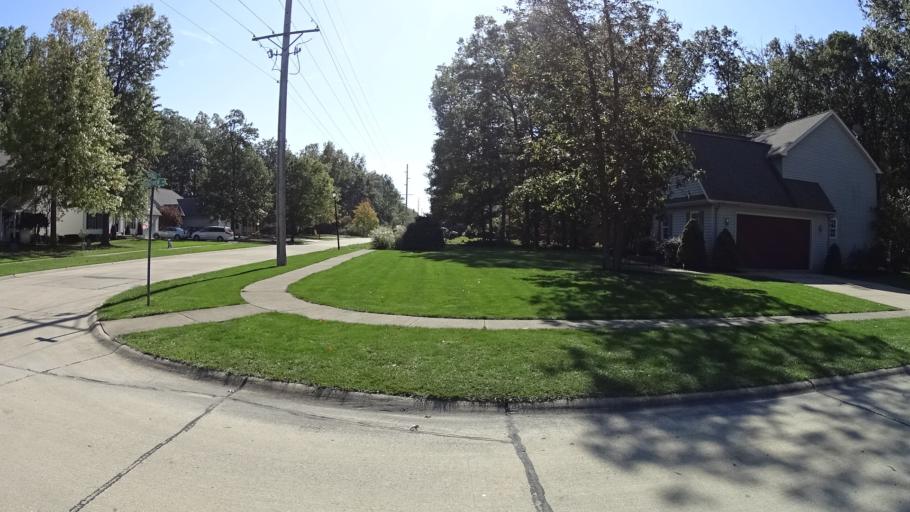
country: US
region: Ohio
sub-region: Lorain County
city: Vermilion-on-the-Lake
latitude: 41.4218
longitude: -82.3332
